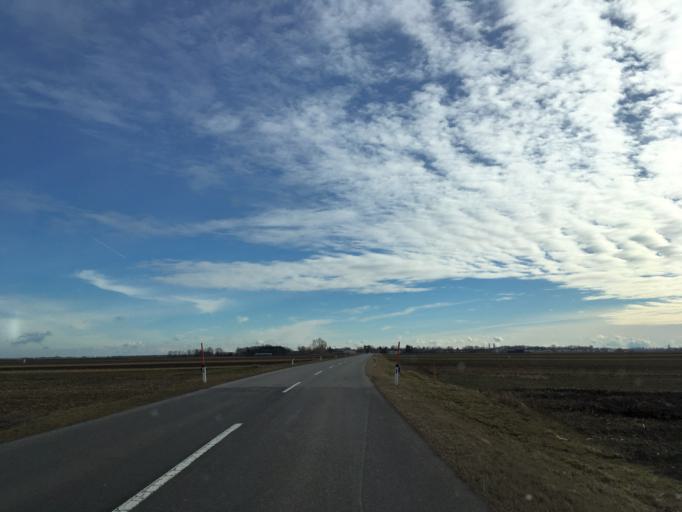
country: AT
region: Burgenland
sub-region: Politischer Bezirk Neusiedl am See
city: Pama
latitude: 48.0585
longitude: 17.0160
